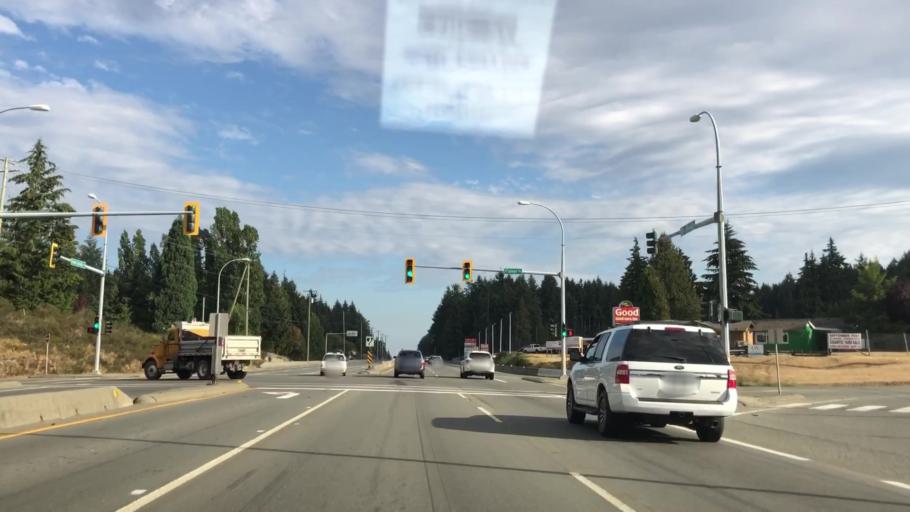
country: CA
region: British Columbia
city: Duncan
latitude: 48.6959
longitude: -123.5916
